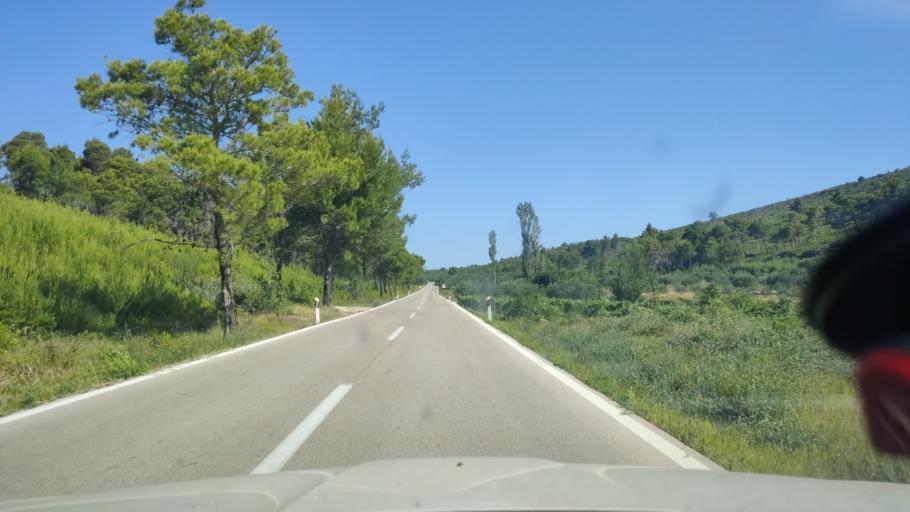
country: HR
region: Sibensko-Kniniska
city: Zaton
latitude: 43.8628
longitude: 15.8908
